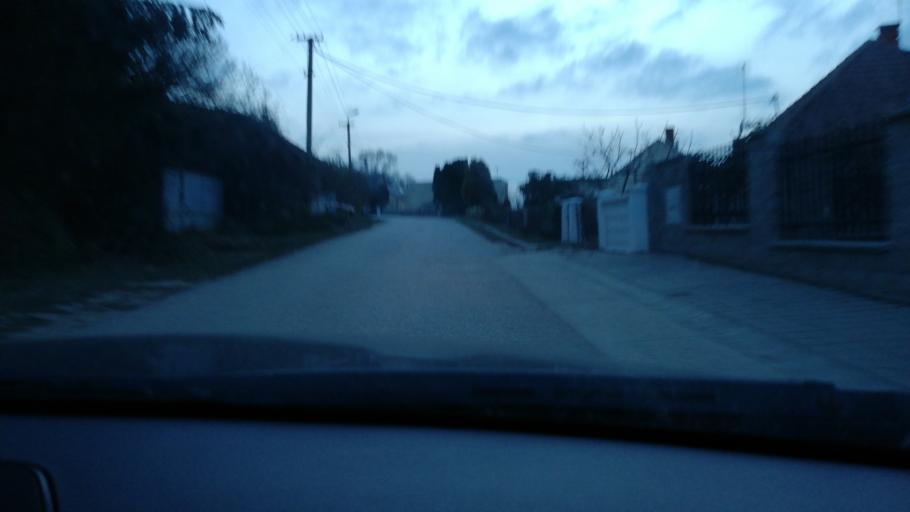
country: SK
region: Nitriansky
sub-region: Okres Nitra
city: Nitra
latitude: 48.3091
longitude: 17.9925
